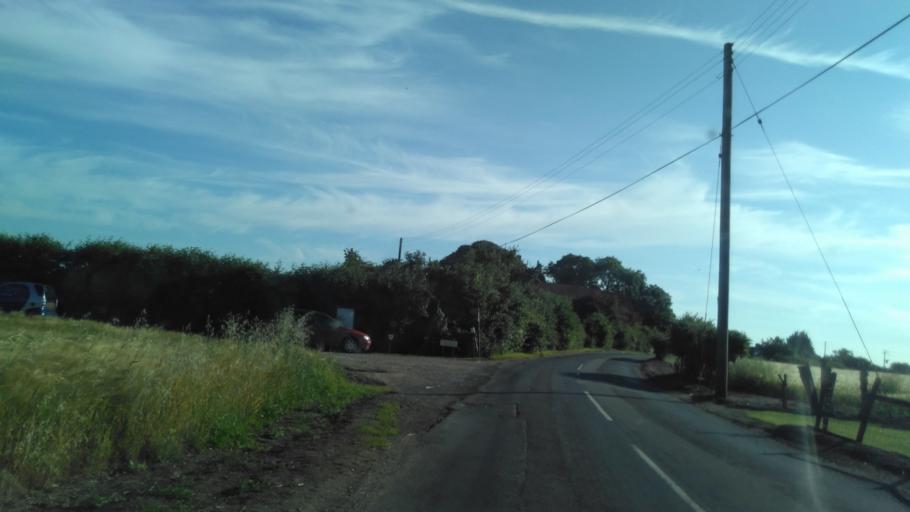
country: GB
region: England
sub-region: Kent
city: Dunkirk
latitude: 51.3251
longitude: 0.9437
